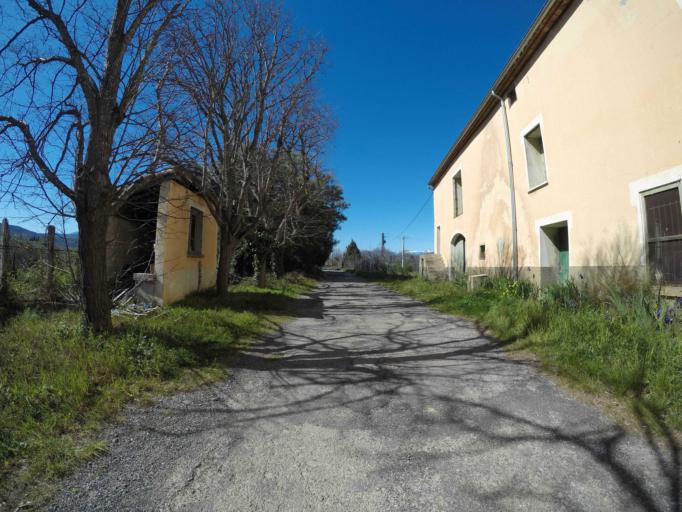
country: FR
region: Languedoc-Roussillon
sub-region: Departement des Pyrenees-Orientales
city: Ille-sur-Tet
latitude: 42.6823
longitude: 2.6483
